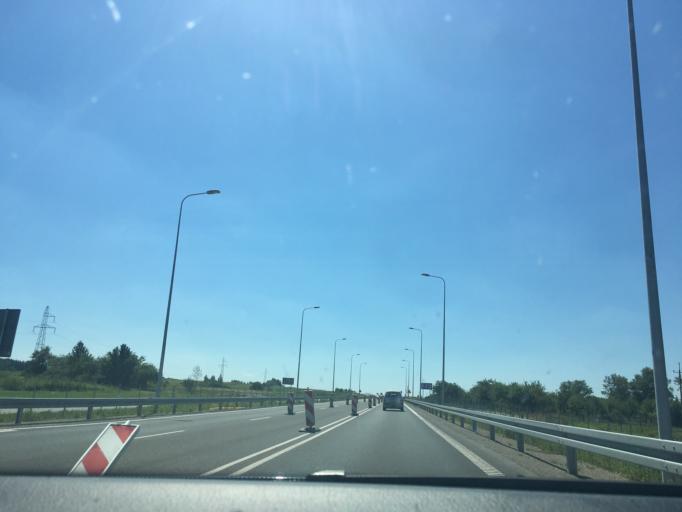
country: PL
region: Subcarpathian Voivodeship
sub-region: Powiat rzeszowski
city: Wolka Podlesna
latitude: 50.1599
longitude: 22.0830
